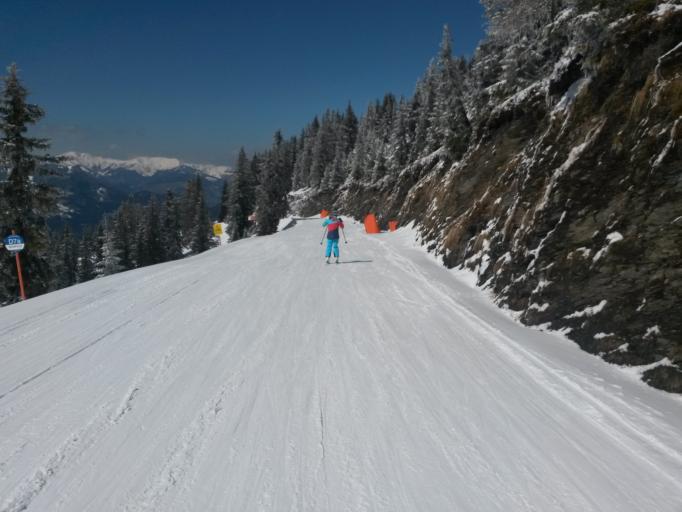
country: AT
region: Salzburg
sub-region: Politischer Bezirk Sankt Johann im Pongau
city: Dorfgastein
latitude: 47.2334
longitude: 13.1458
